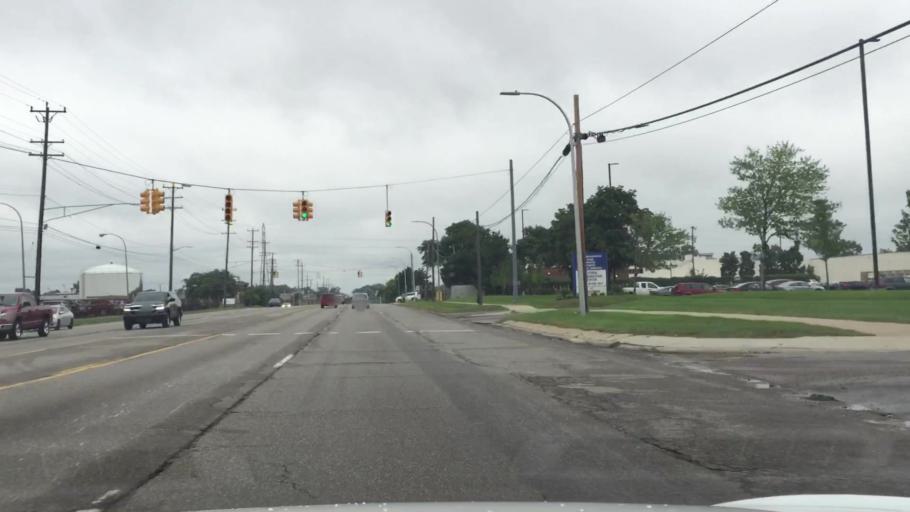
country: US
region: Michigan
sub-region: Wayne County
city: Livonia
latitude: 42.3729
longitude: -83.3331
